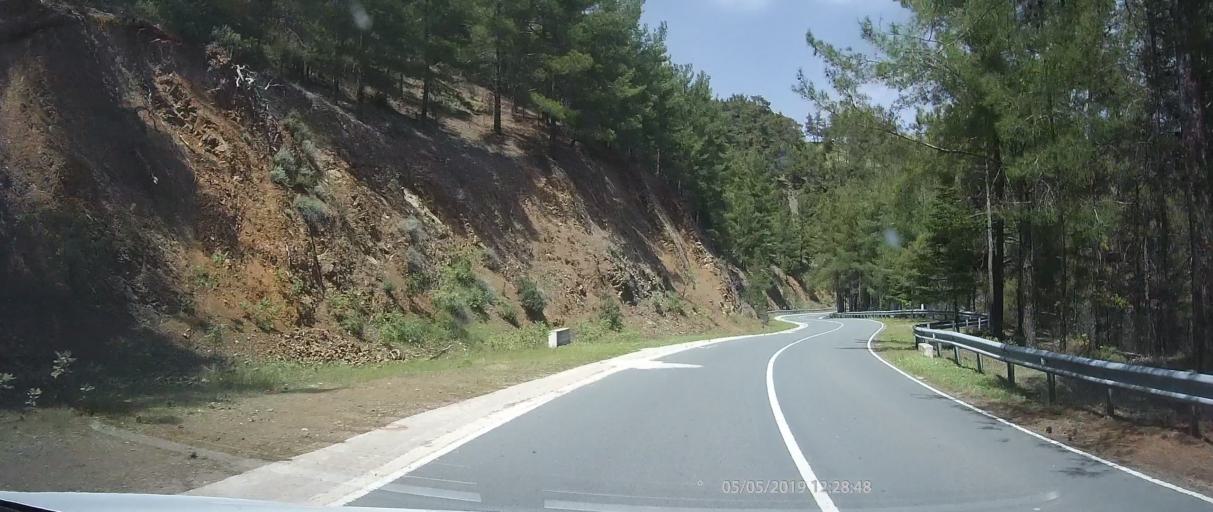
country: CY
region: Lefkosia
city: Kakopetria
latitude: 34.9799
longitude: 32.7435
